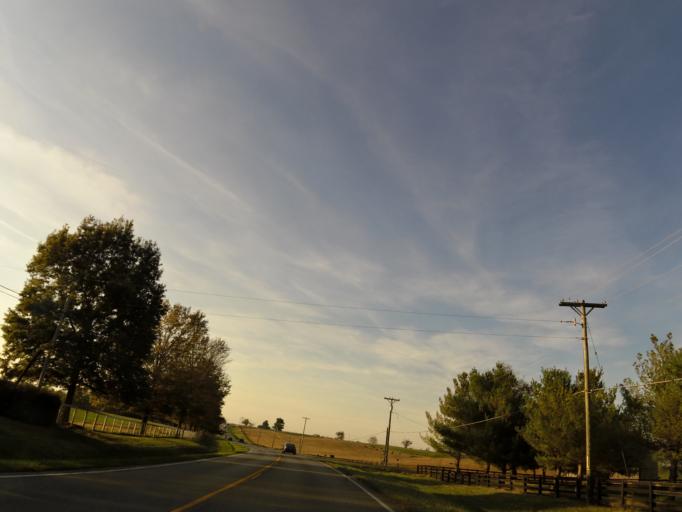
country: US
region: Kentucky
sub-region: Garrard County
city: Lancaster
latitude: 37.6818
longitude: -84.6501
